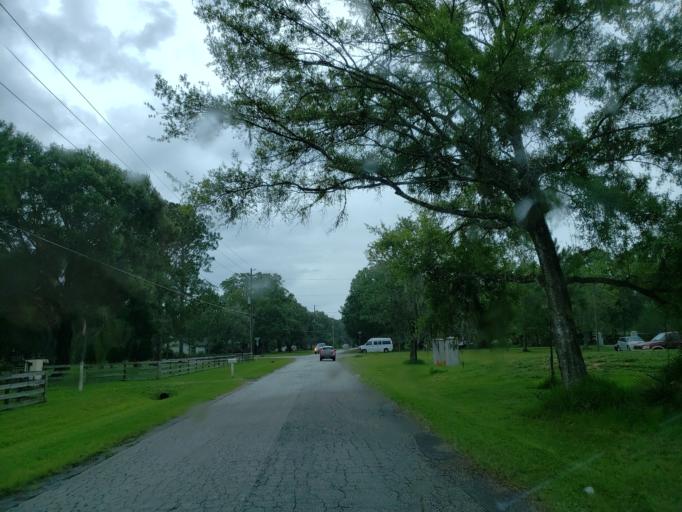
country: US
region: Florida
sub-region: Pasco County
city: Wesley Chapel
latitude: 28.2648
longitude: -82.3504
